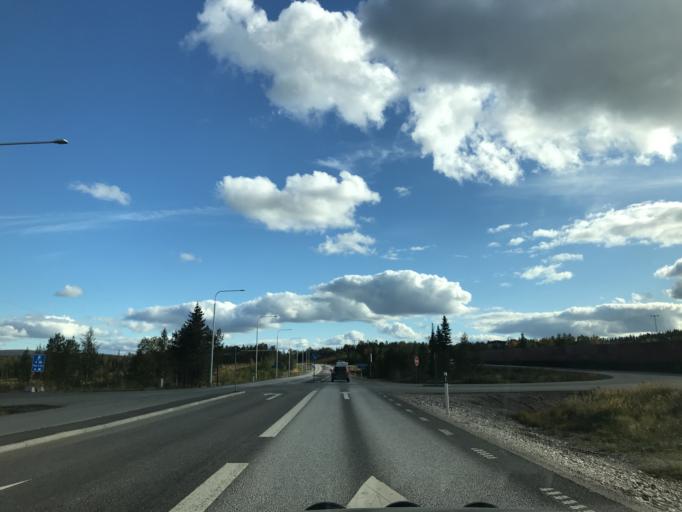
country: SE
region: Norrbotten
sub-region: Gallivare Kommun
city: Malmberget
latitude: 67.6527
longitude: 21.0160
